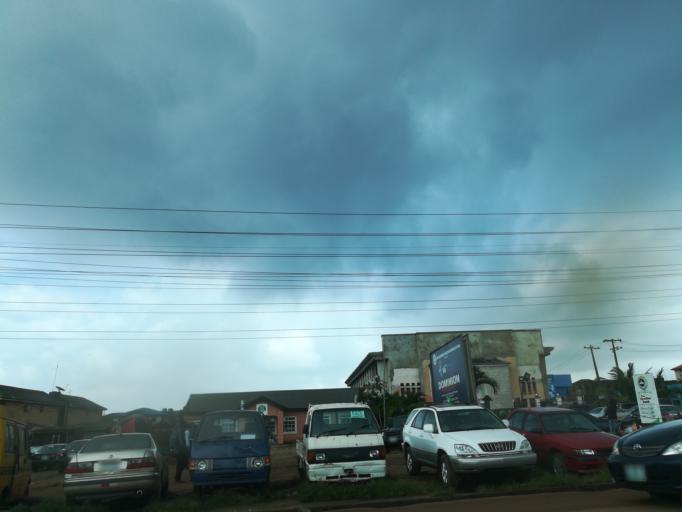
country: NG
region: Lagos
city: Ikorodu
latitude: 6.6607
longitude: 3.5195
